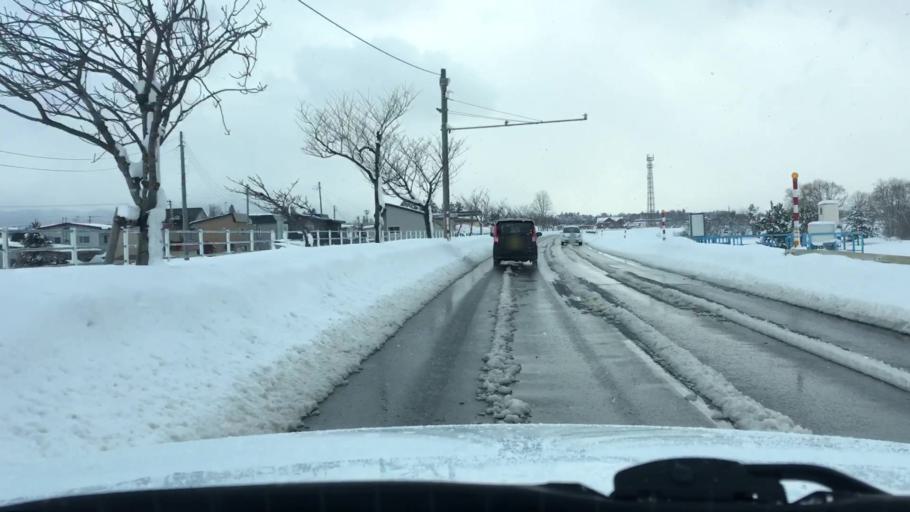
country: JP
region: Aomori
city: Hirosaki
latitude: 40.6253
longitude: 140.4738
